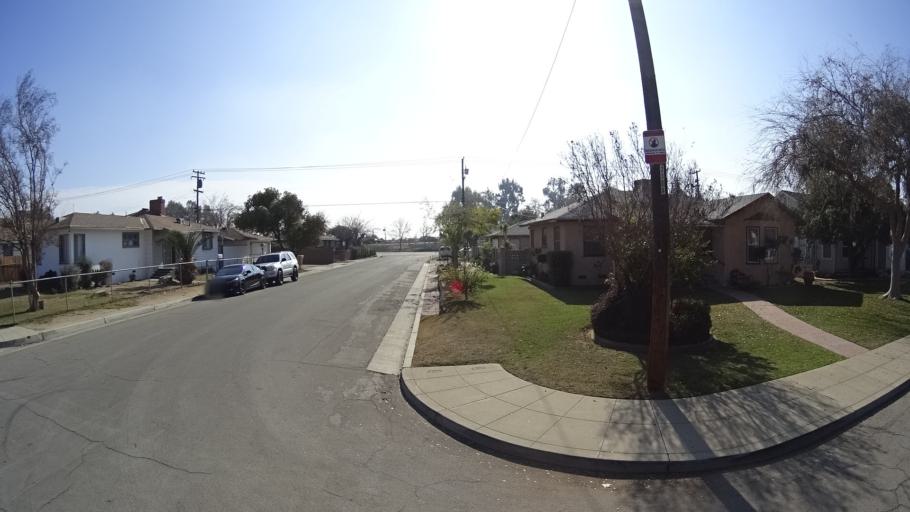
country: US
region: California
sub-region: Kern County
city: Bakersfield
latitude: 35.3849
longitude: -119.0008
